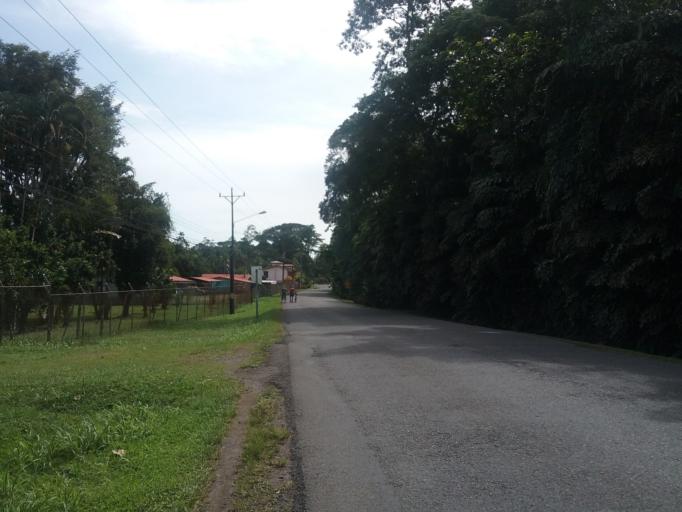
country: CR
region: Limon
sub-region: Canton de Pococi
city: Guapiles
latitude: 10.3204
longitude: -83.9127
